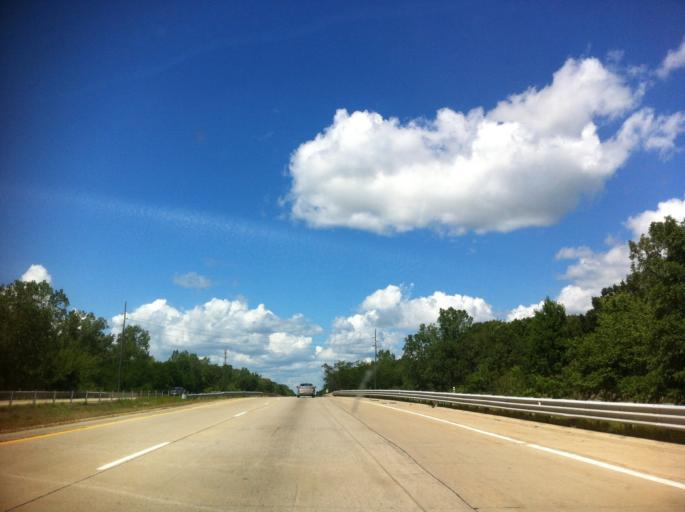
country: US
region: Michigan
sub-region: Monroe County
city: Dundee
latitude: 41.9130
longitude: -83.6619
